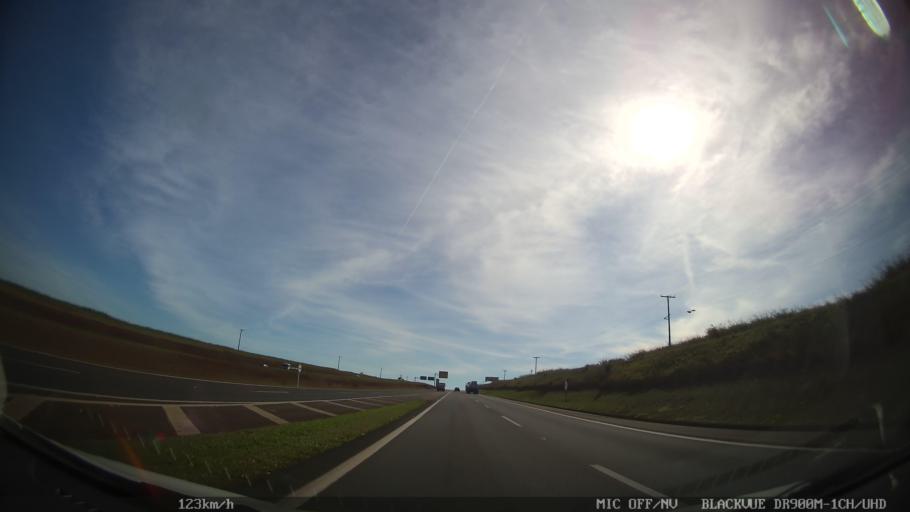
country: BR
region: Sao Paulo
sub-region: Cordeiropolis
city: Cordeiropolis
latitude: -22.4775
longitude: -47.3993
